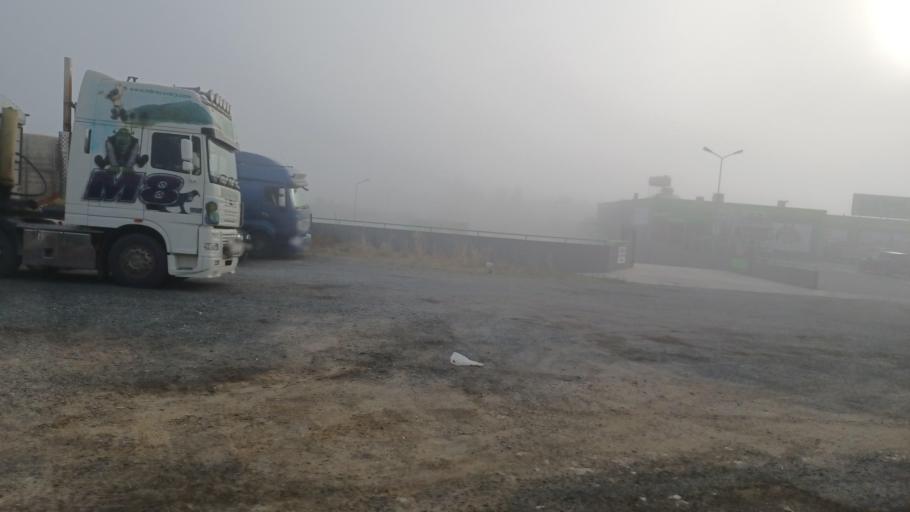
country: CY
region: Ammochostos
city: Acheritou
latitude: 35.0843
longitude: 33.8774
